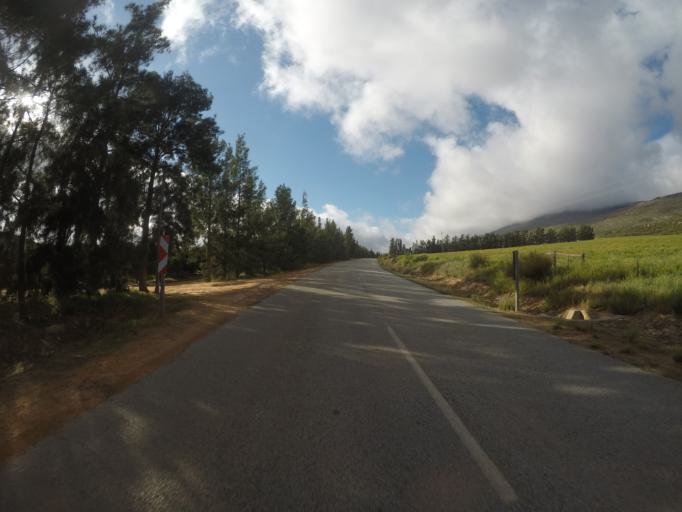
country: ZA
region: Western Cape
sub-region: West Coast District Municipality
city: Clanwilliam
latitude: -32.3485
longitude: 18.8458
